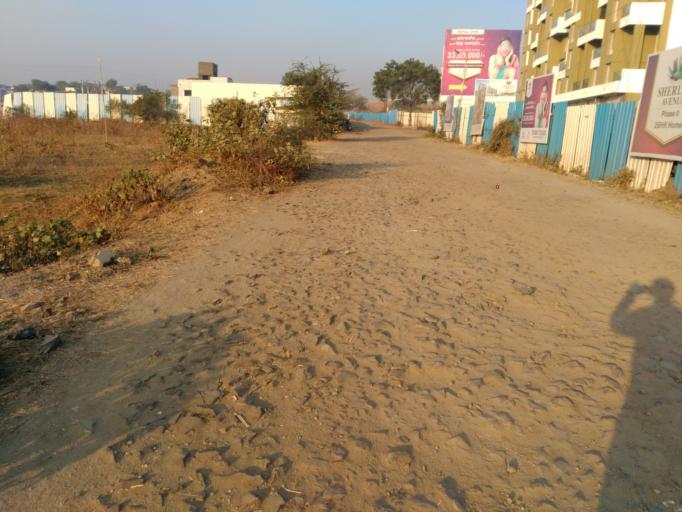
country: IN
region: Maharashtra
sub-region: Pune Division
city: Pune
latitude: 18.4418
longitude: 73.9050
